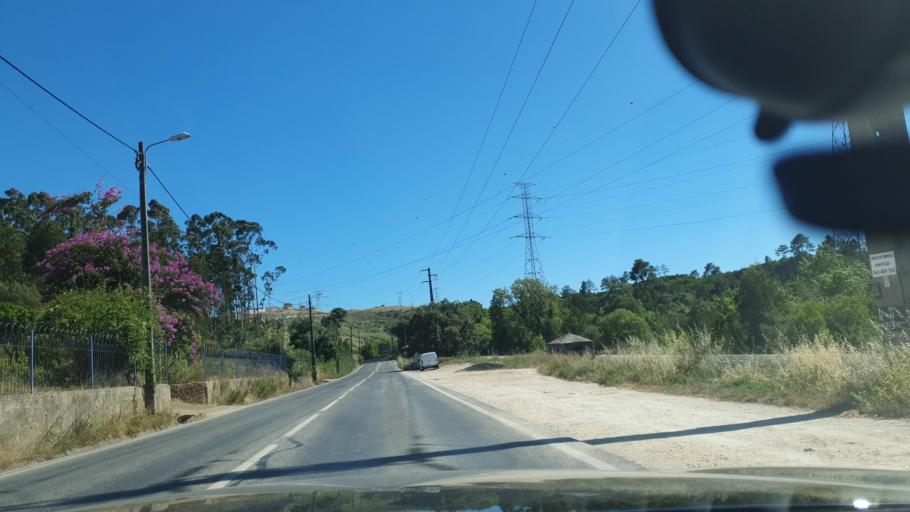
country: PT
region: Lisbon
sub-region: Sintra
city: Belas
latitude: 38.7905
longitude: -9.2439
